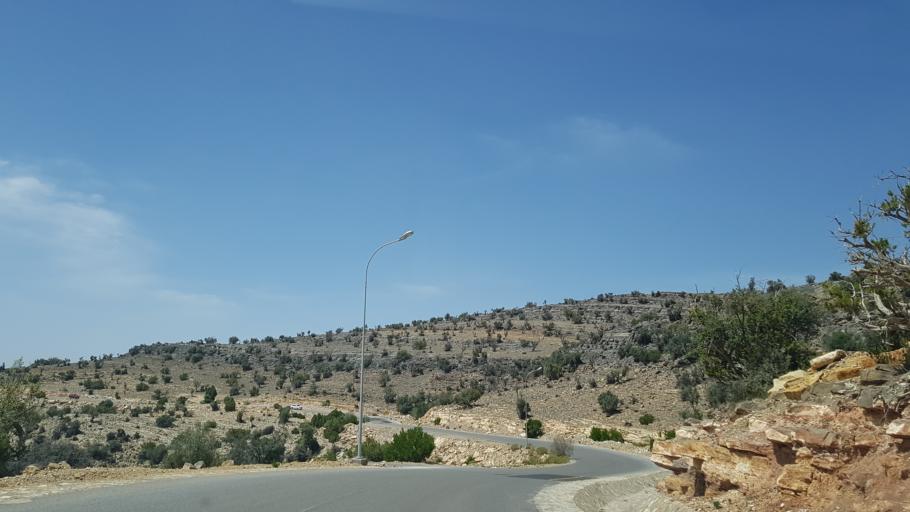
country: OM
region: Al Batinah
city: Bayt al `Awabi
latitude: 23.1374
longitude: 57.5949
